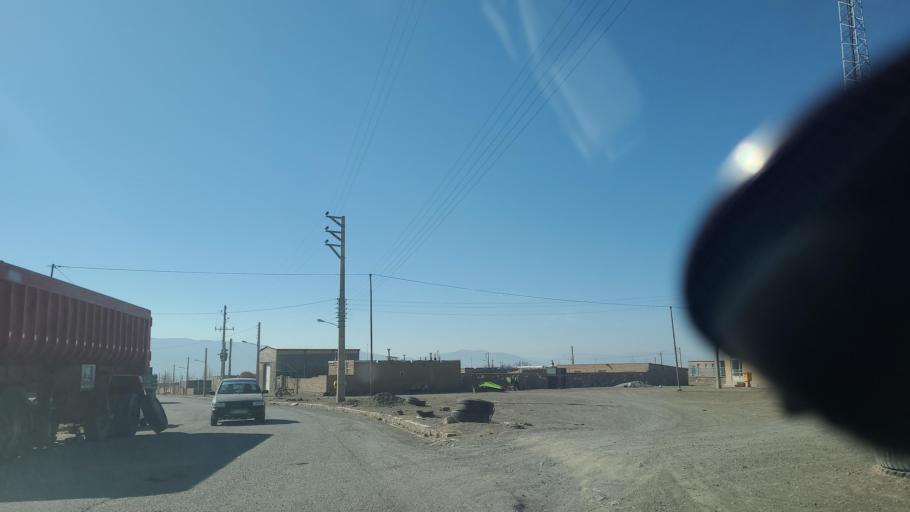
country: IR
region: Razavi Khorasan
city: Dowlatabad
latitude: 35.6207
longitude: 59.4777
